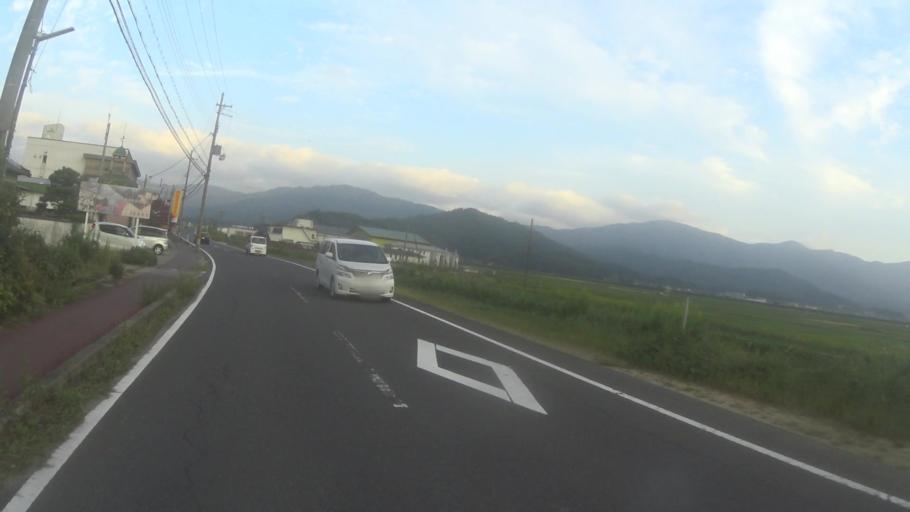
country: JP
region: Kyoto
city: Miyazu
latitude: 35.5290
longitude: 135.1012
